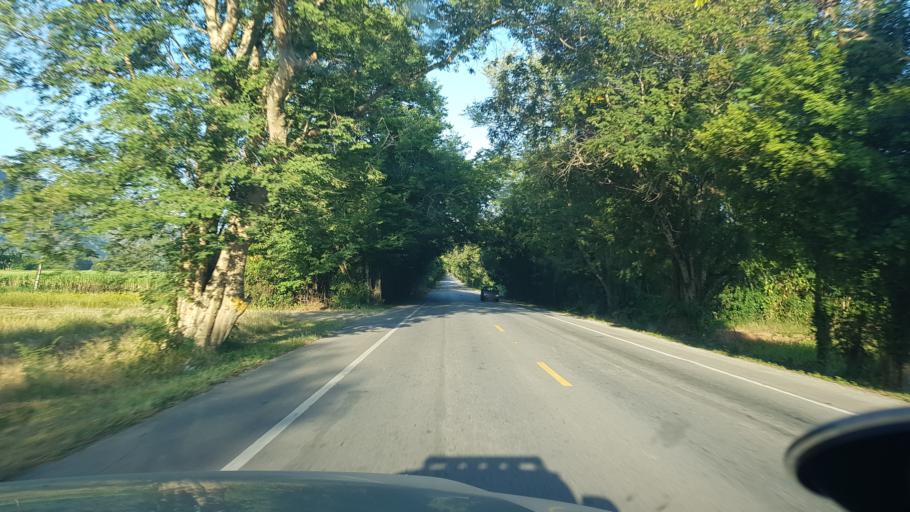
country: TH
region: Khon Kaen
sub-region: Amphoe Phu Pha Man
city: Phu Pha Man
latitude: 16.6196
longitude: 101.8695
